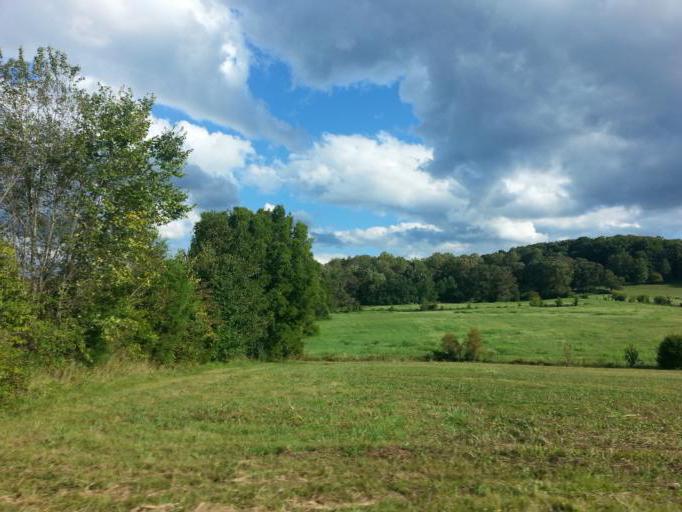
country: US
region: Tennessee
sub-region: Knox County
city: Mascot
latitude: 36.0727
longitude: -83.8361
